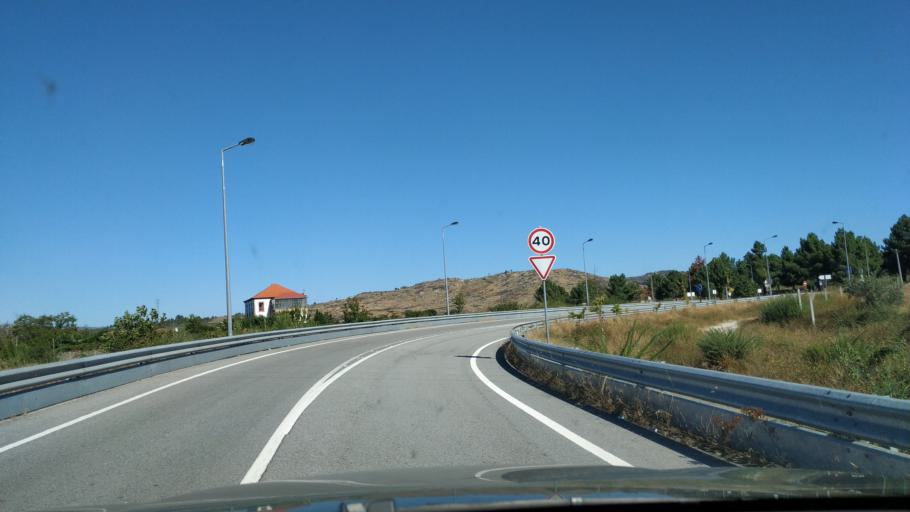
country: PT
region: Vila Real
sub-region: Sabrosa
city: Vilela
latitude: 41.2674
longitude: -7.6346
